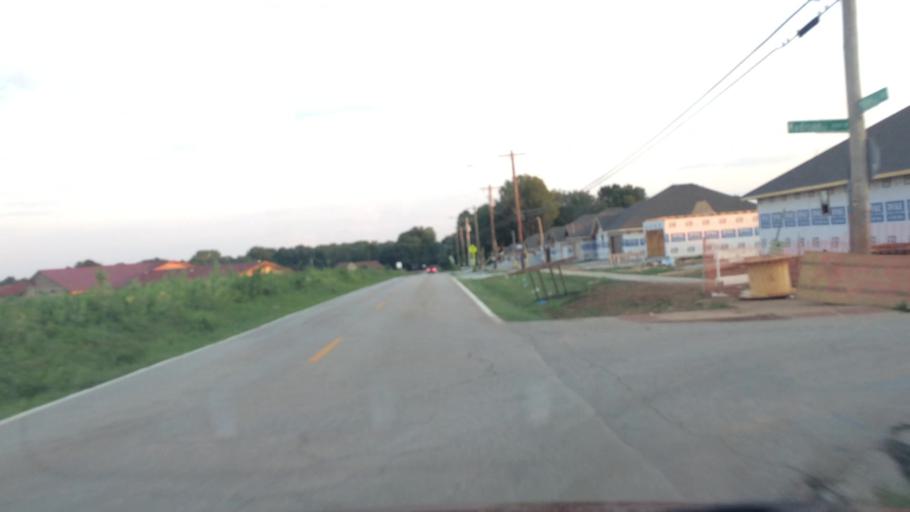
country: US
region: Missouri
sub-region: Greene County
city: Springfield
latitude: 37.2016
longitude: -93.3743
